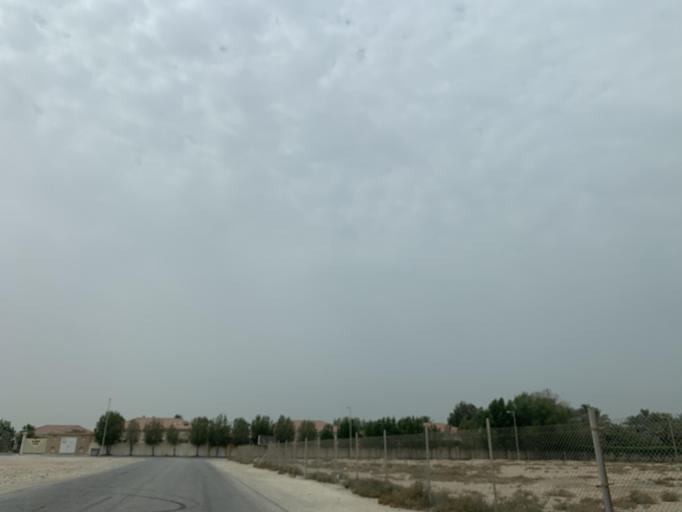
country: BH
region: Central Governorate
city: Madinat Hamad
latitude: 26.1800
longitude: 50.4712
